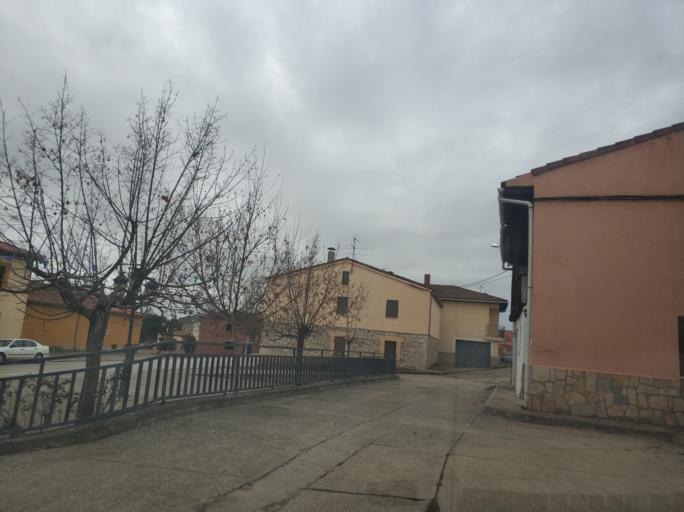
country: ES
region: Castille and Leon
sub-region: Provincia de Soria
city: Santa Maria de las Hoyas
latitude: 41.7706
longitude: -3.1430
